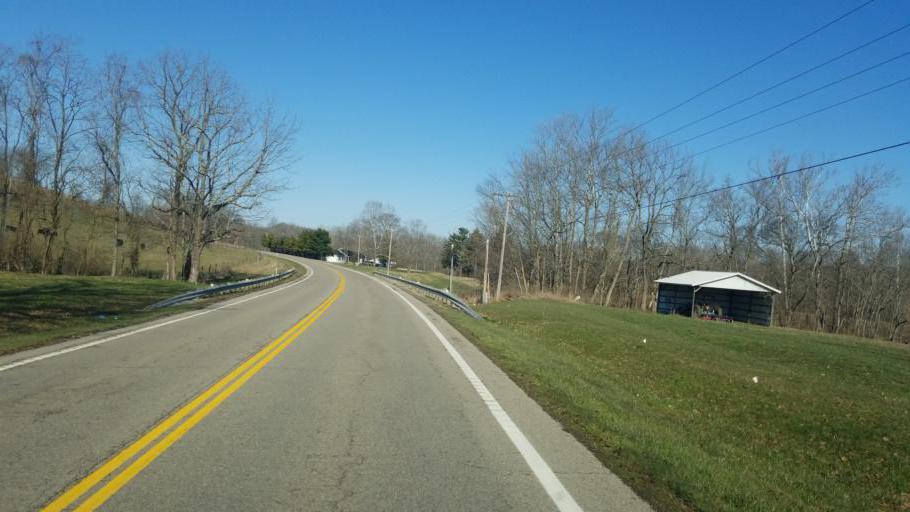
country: US
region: Ohio
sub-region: Highland County
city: Greenfield
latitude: 39.2297
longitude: -83.3234
